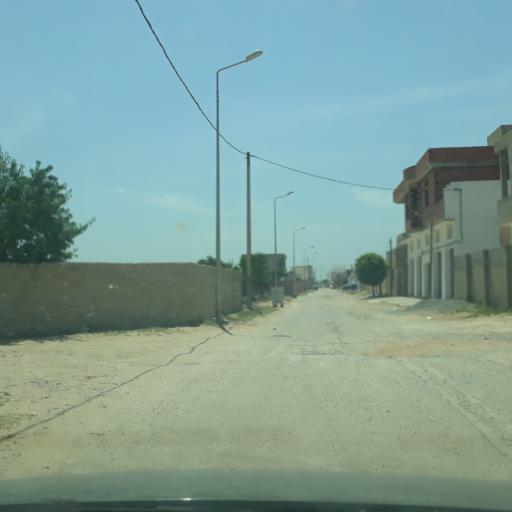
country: TN
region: Safaqis
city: Al Qarmadah
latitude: 34.8262
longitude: 10.7784
